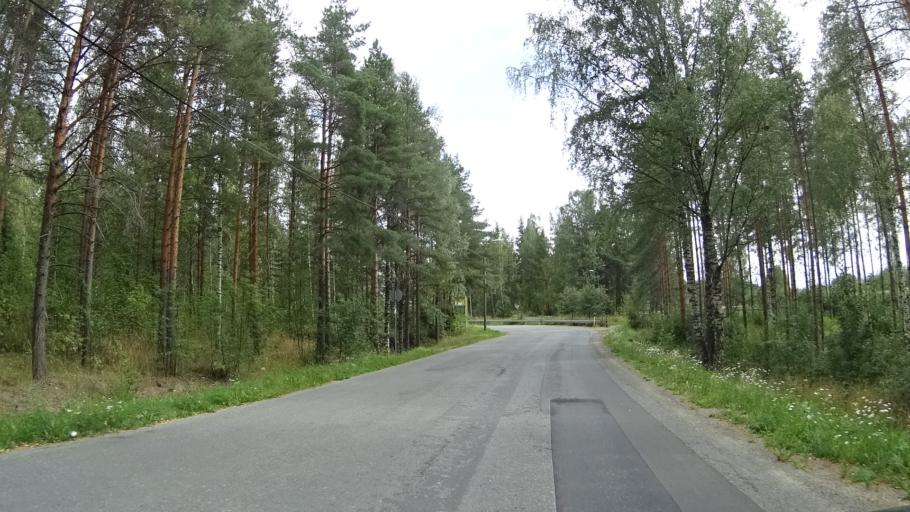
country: FI
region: Pirkanmaa
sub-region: Tampere
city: Kangasala
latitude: 61.4463
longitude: 24.1226
